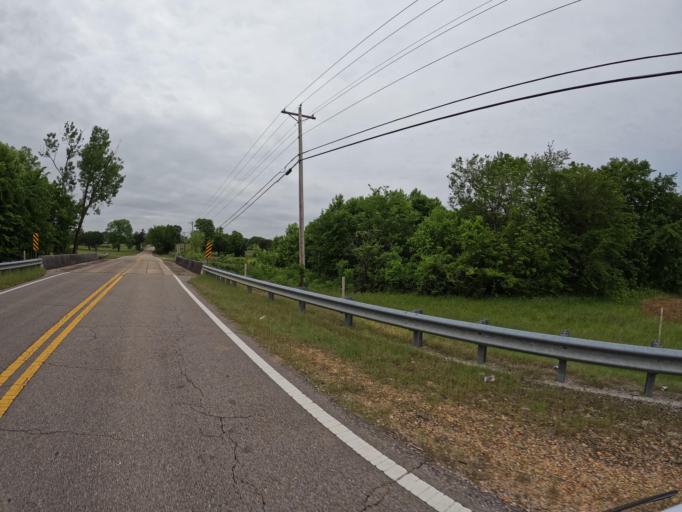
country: US
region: Mississippi
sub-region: Lee County
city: Tupelo
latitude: 34.2911
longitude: -88.7642
